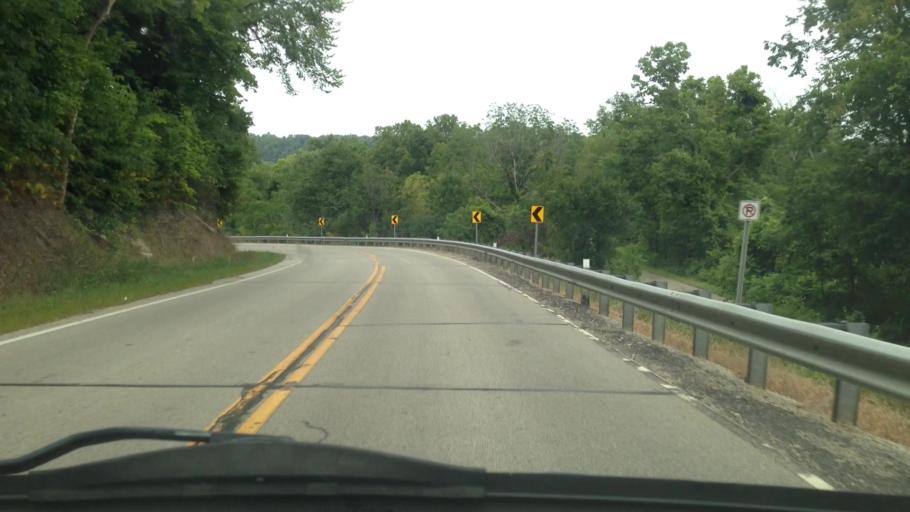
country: US
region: Minnesota
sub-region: Fillmore County
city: Preston
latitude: 43.7348
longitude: -91.9639
